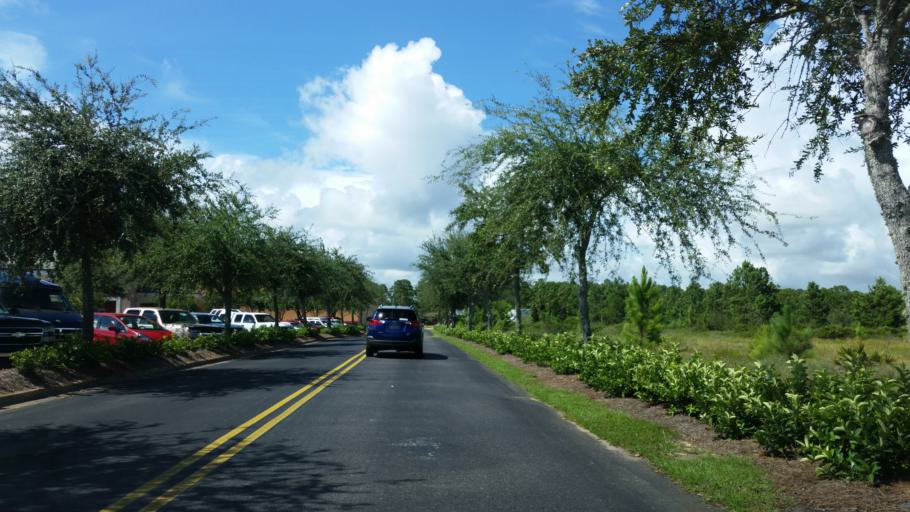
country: US
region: Florida
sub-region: Santa Rosa County
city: Navarre
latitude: 30.4027
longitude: -86.8779
